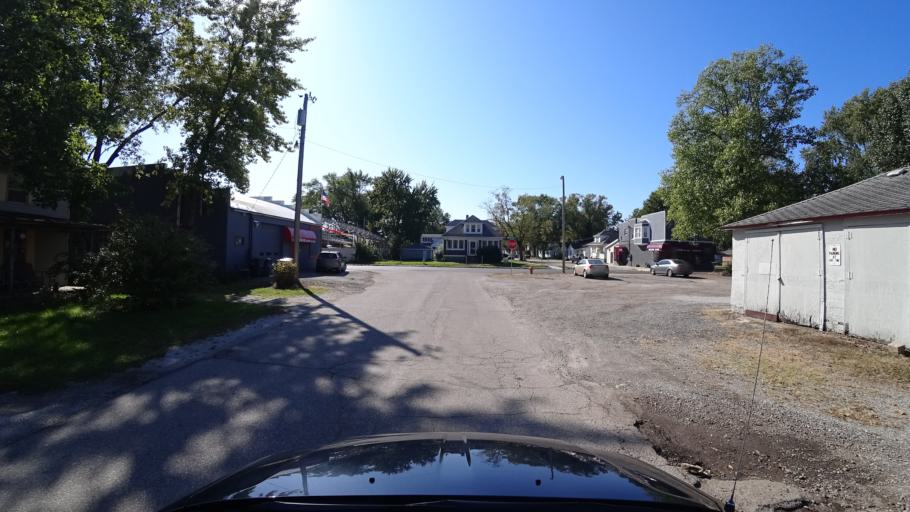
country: US
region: Indiana
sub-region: LaPorte County
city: Michigan City
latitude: 41.7064
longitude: -86.8894
